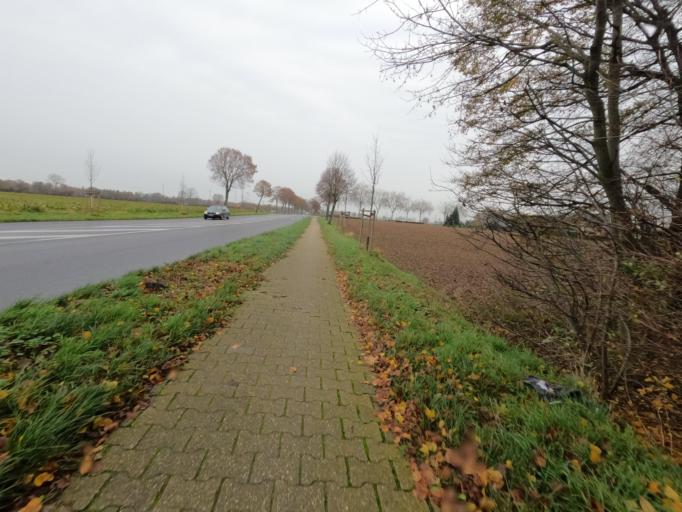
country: DE
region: North Rhine-Westphalia
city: Geilenkirchen
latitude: 50.9944
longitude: 6.1194
